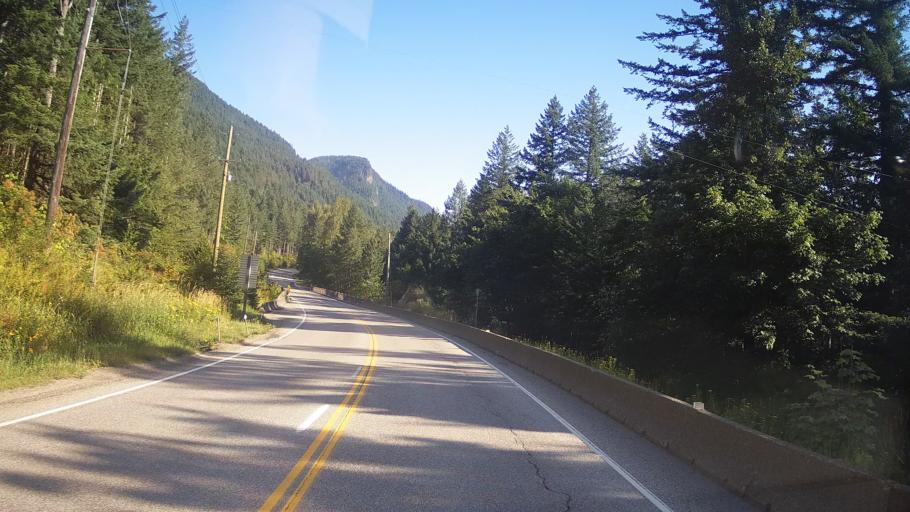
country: CA
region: British Columbia
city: Hope
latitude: 49.4292
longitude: -121.4378
